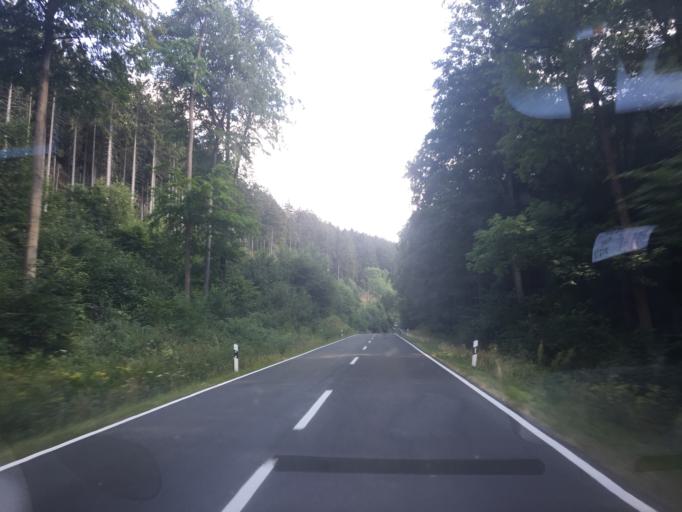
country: DE
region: Saxony-Anhalt
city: Darlingerode
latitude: 51.8003
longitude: 10.7343
